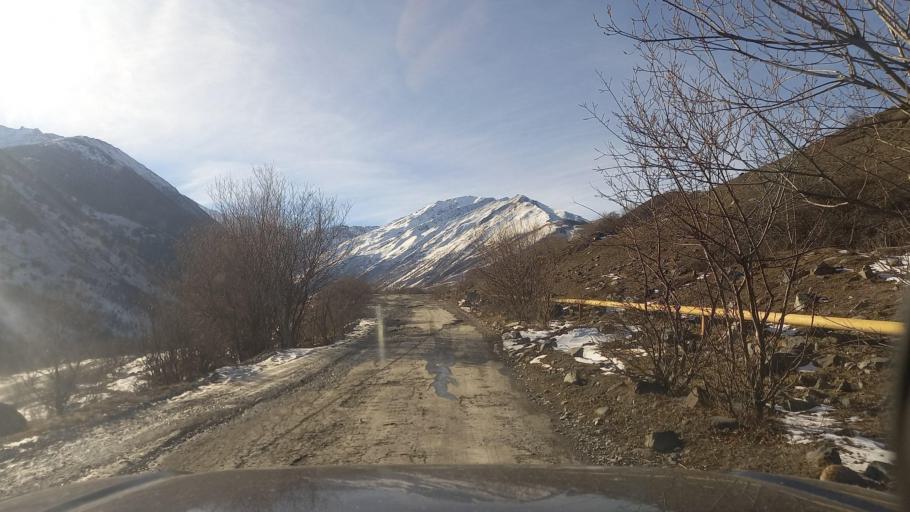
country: RU
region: Ingushetiya
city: Dzhayrakh
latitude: 42.8411
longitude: 44.5136
